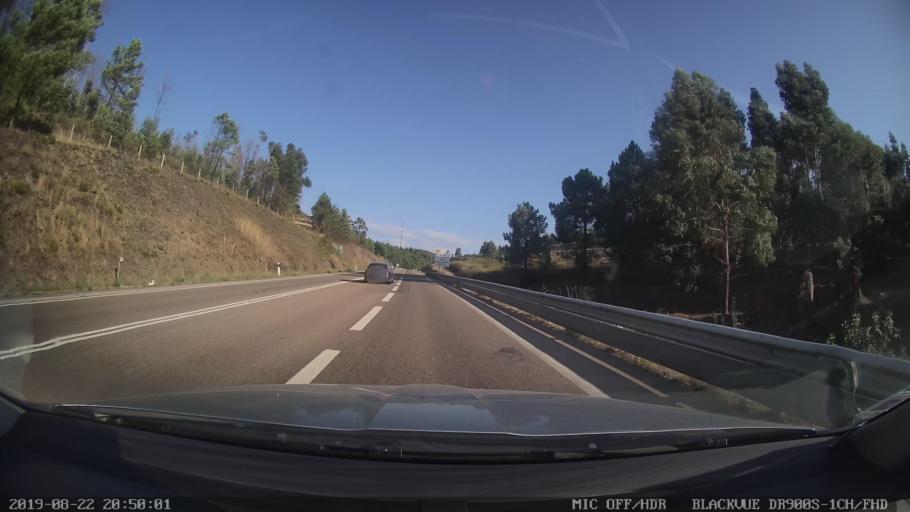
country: PT
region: Castelo Branco
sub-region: Proenca-A-Nova
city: Proenca-a-Nova
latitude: 39.7499
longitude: -7.9350
